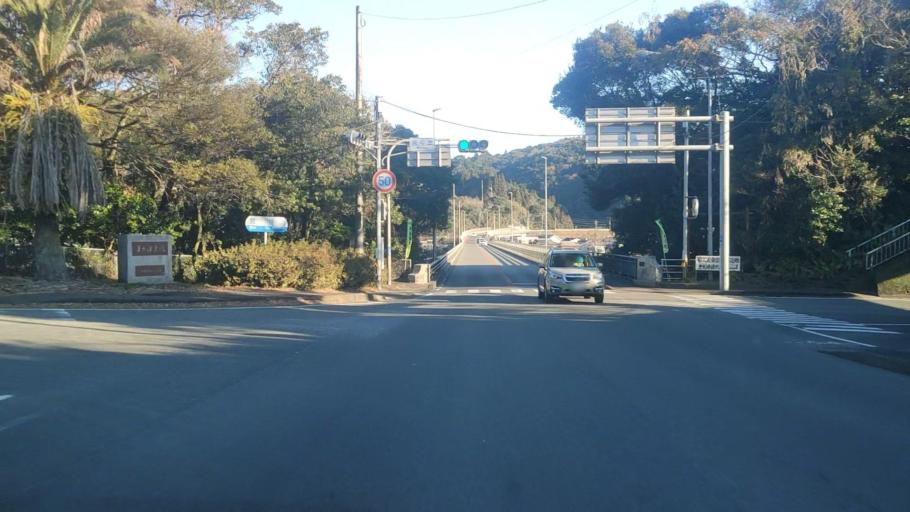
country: JP
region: Miyazaki
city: Takanabe
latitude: 32.3380
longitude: 131.6112
